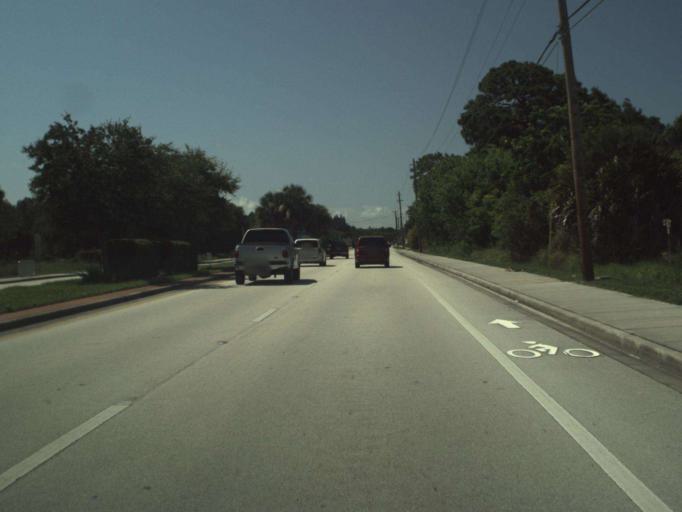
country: US
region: Florida
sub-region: Indian River County
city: Winter Beach
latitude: 27.7449
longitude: -80.4329
